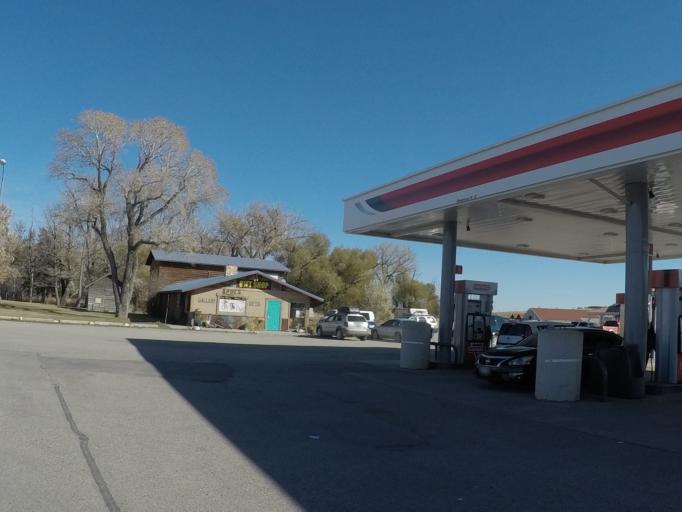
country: US
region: Montana
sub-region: Sweet Grass County
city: Big Timber
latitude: 45.8273
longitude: -109.9720
